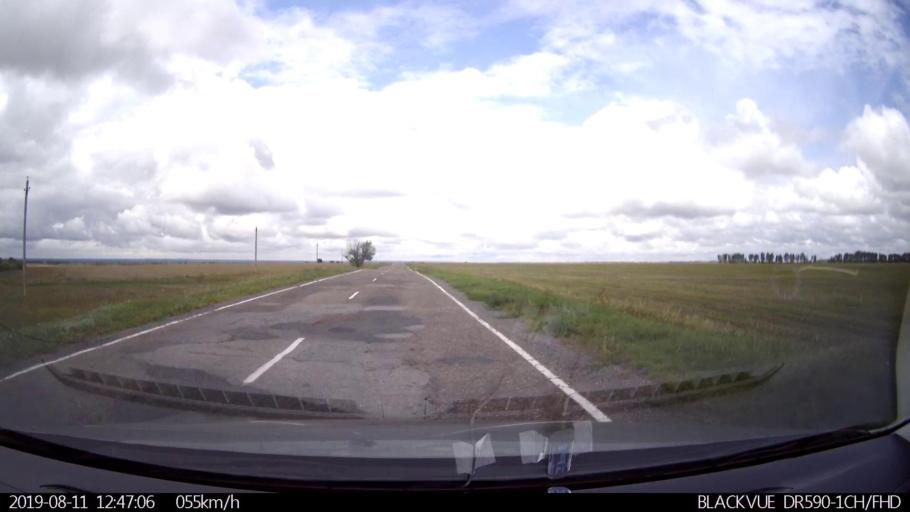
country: RU
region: Ulyanovsk
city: Ignatovka
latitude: 53.8679
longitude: 47.7119
